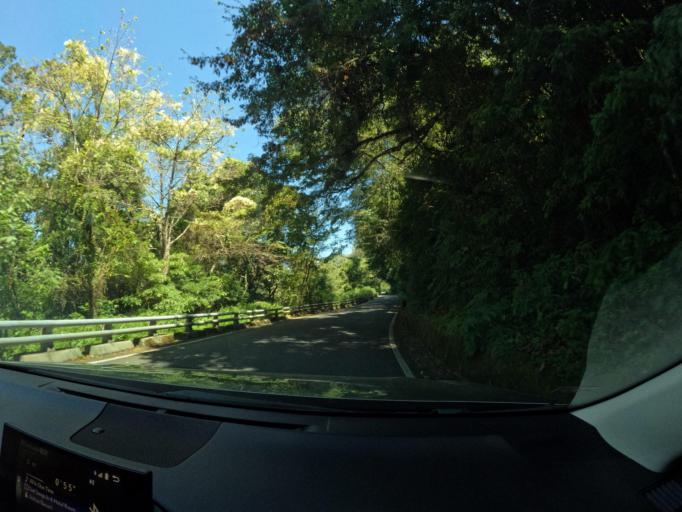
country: TW
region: Taiwan
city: Yujing
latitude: 23.2808
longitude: 120.8950
